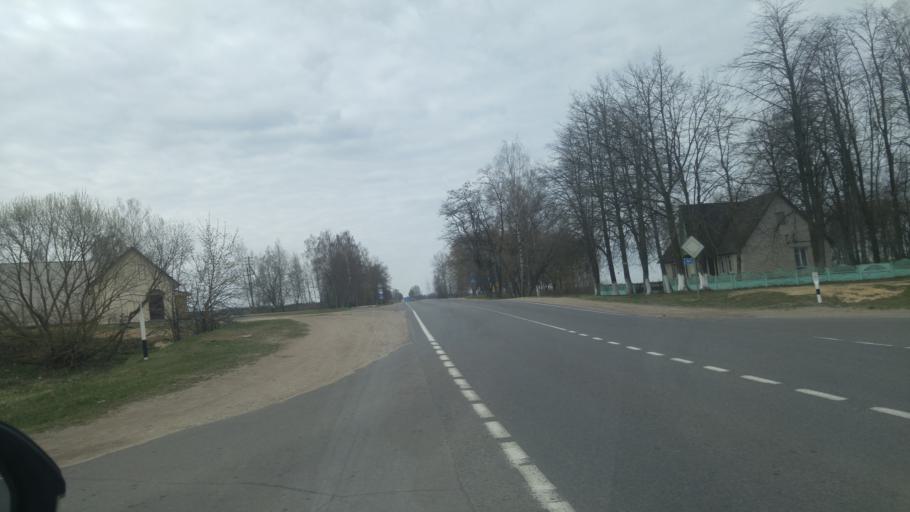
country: BY
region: Minsk
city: Pukhavichy
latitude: 53.5868
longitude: 28.2262
